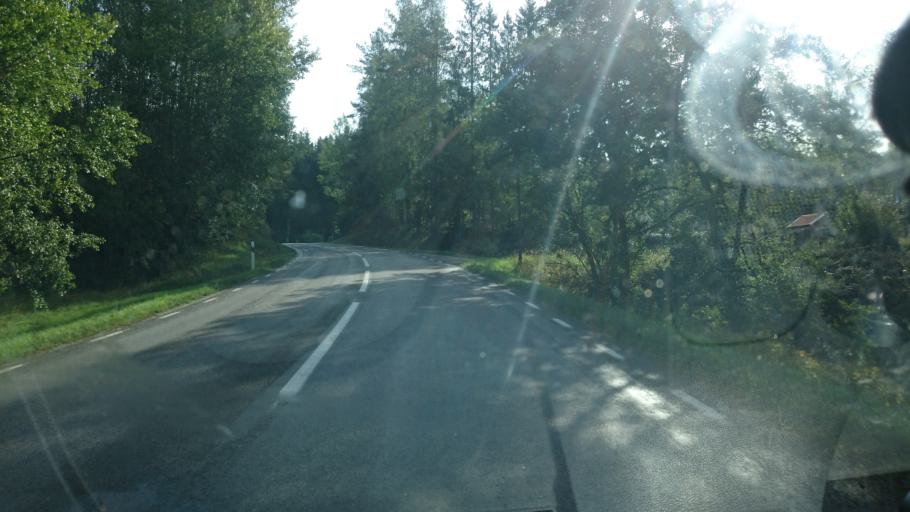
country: SE
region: Vaestra Goetaland
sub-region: Vanersborgs Kommun
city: Vargon
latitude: 58.2537
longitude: 12.4106
